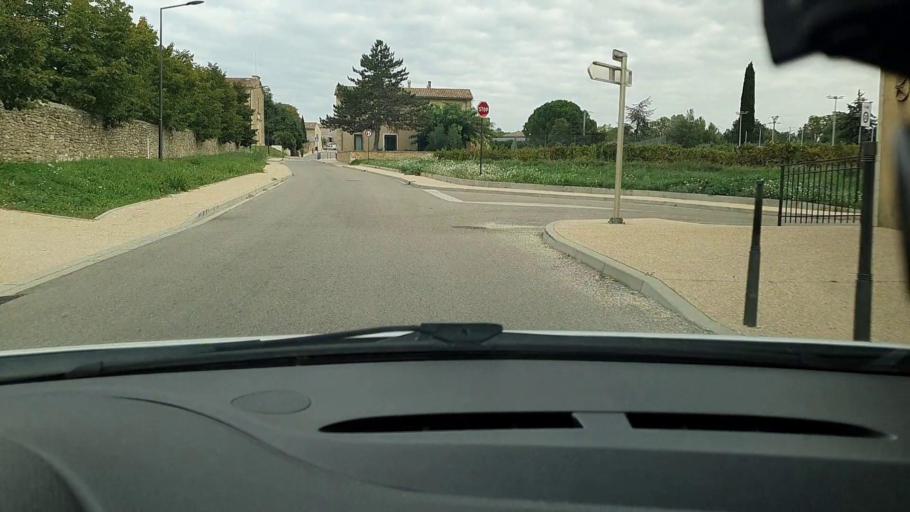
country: FR
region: Languedoc-Roussillon
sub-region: Departement du Gard
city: Saint-Chaptes
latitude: 44.0407
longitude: 4.2981
